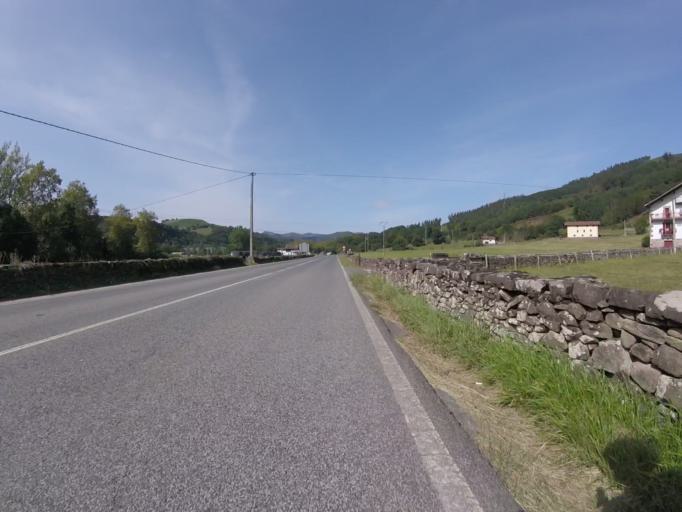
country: ES
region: Navarre
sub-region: Provincia de Navarra
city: Doneztebe
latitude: 43.1321
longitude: -1.6430
